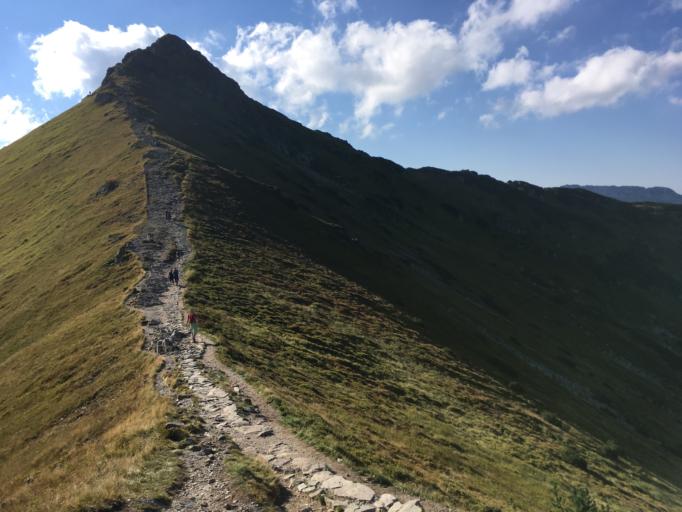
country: PL
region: Lesser Poland Voivodeship
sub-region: Powiat tatrzanski
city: Zakopane
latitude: 49.2314
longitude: 19.9623
